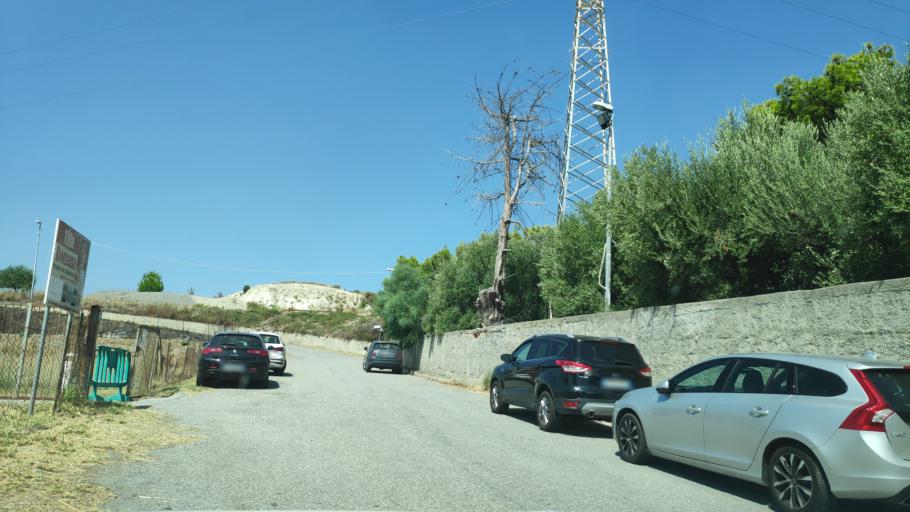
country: IT
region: Calabria
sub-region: Provincia di Reggio Calabria
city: Bianco
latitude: 38.1191
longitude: 16.1584
